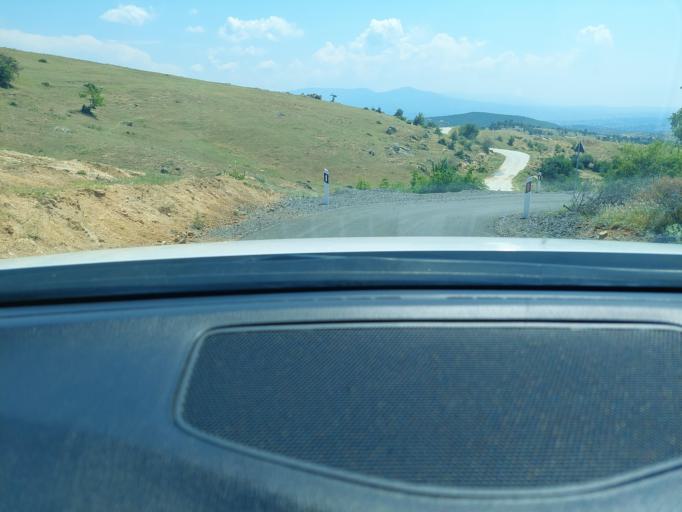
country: MK
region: Radovis
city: Radovish
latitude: 41.6592
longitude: 22.4099
